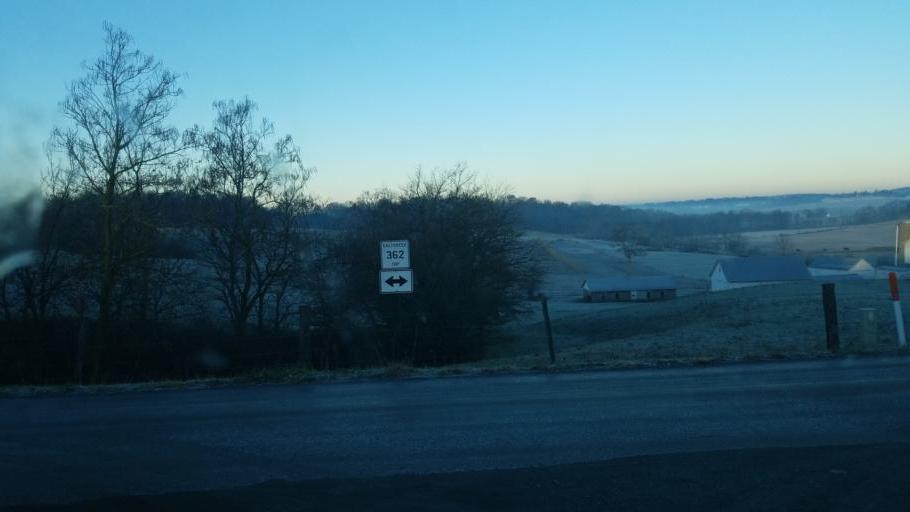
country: US
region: Ohio
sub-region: Holmes County
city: Millersburg
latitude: 40.6075
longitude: -81.8003
